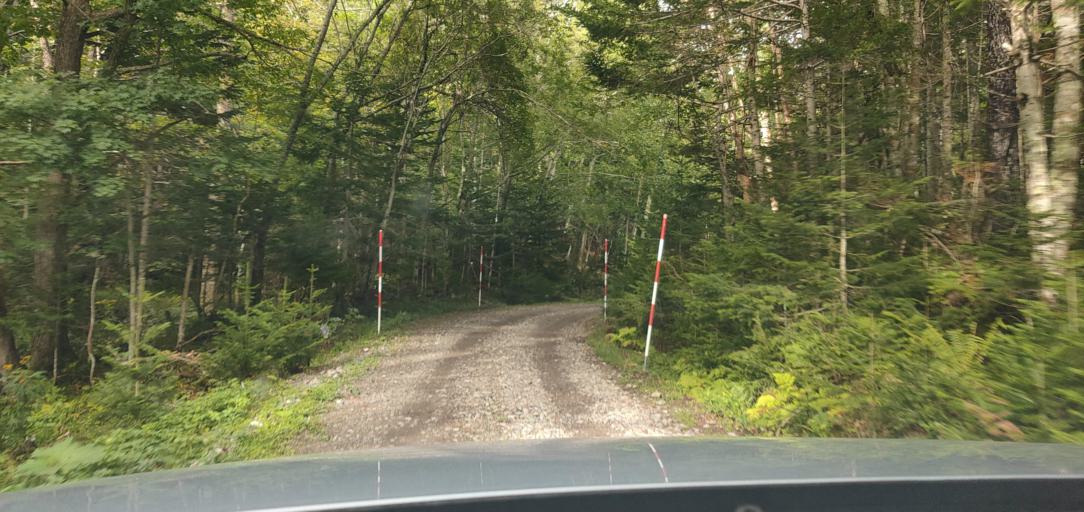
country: JP
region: Hokkaido
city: Kitami
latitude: 43.3719
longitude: 143.9572
